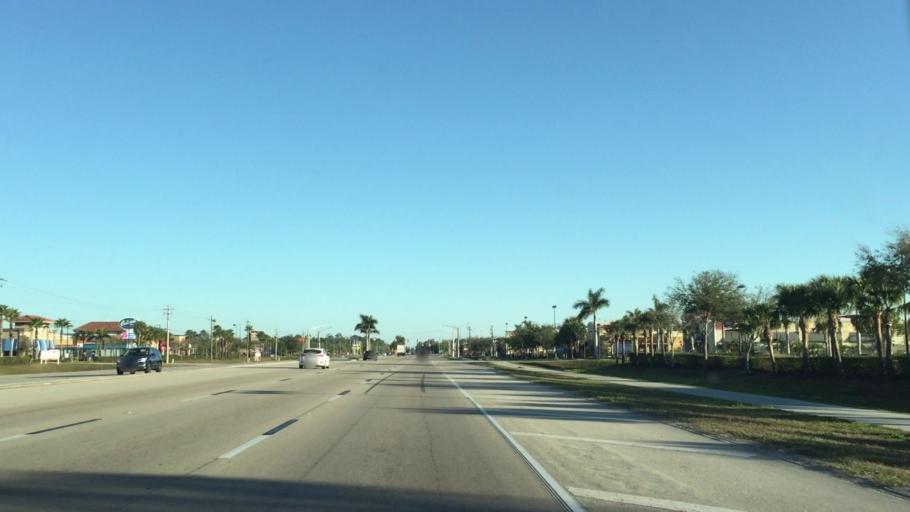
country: US
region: Florida
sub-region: Lee County
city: Fort Myers
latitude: 26.6059
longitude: -81.8111
